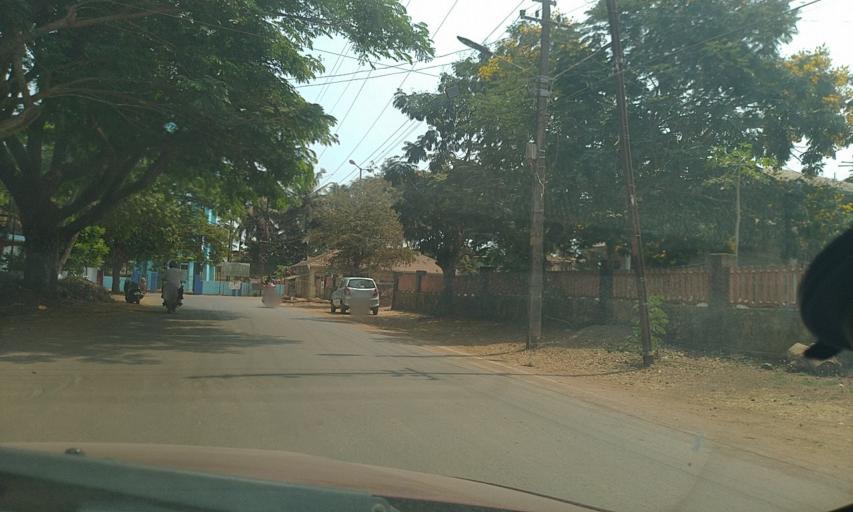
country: IN
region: Goa
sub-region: North Goa
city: Panaji
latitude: 15.5214
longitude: 73.8315
